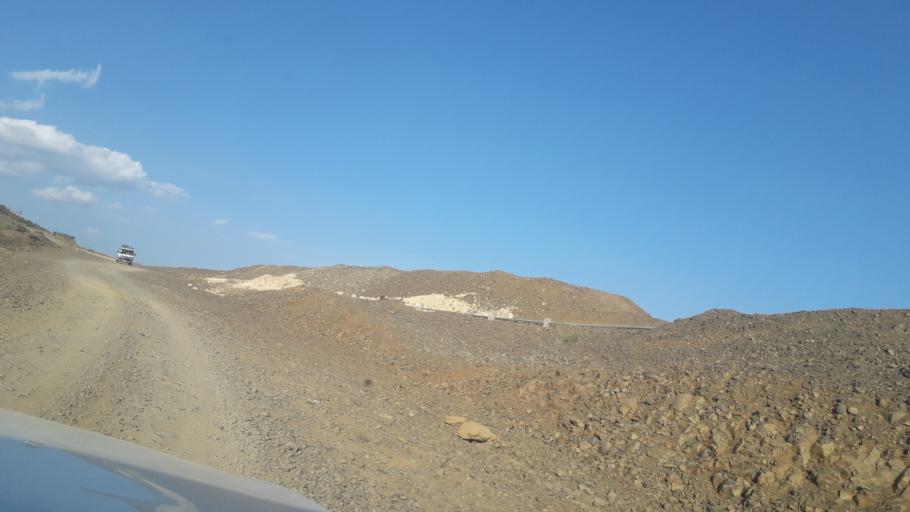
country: ET
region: Amhara
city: Dese
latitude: 11.5222
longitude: 39.2491
